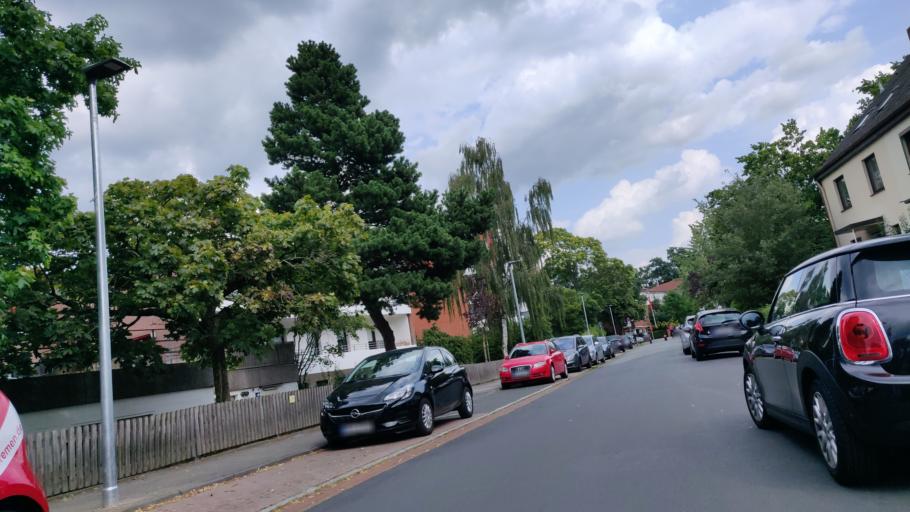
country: DE
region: Lower Saxony
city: Lilienthal
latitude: 53.0998
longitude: 8.8794
